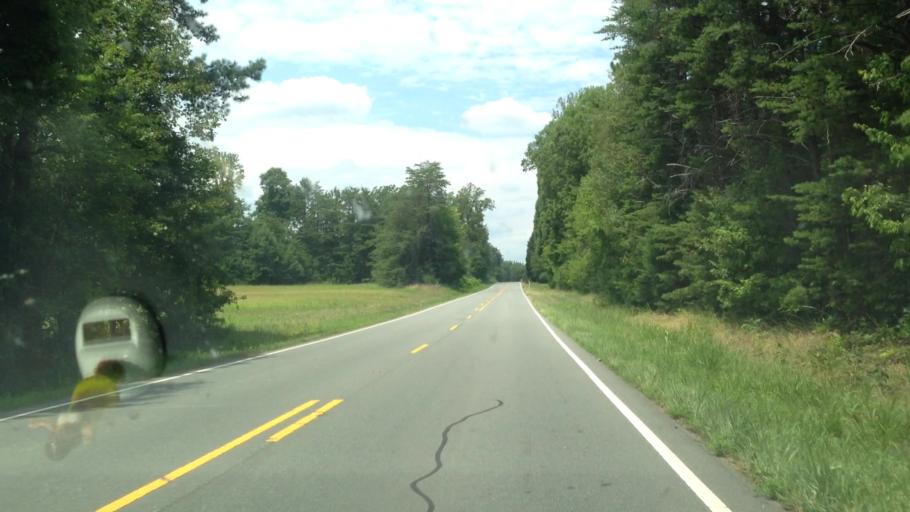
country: US
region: North Carolina
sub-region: Stokes County
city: Walnut Cove
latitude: 36.3649
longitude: -80.0662
